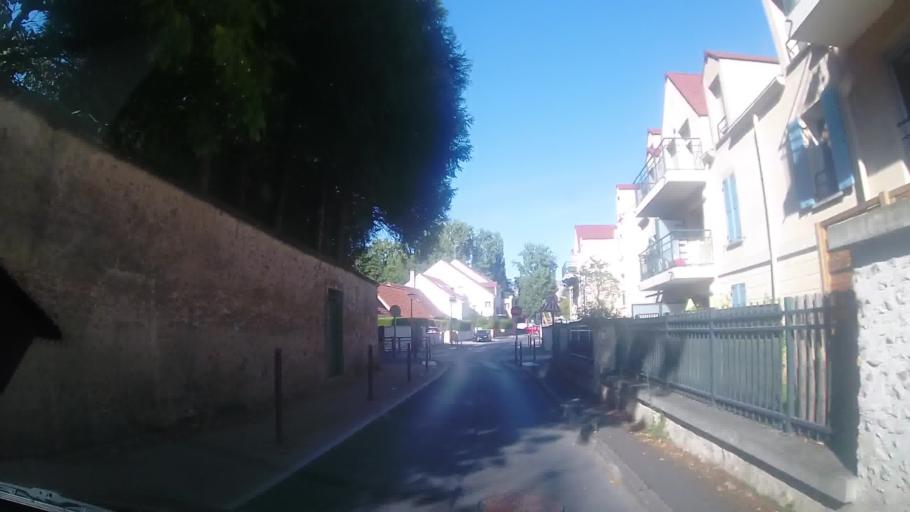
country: FR
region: Ile-de-France
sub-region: Departement de l'Essonne
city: Dourdan
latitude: 48.5290
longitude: 2.0061
